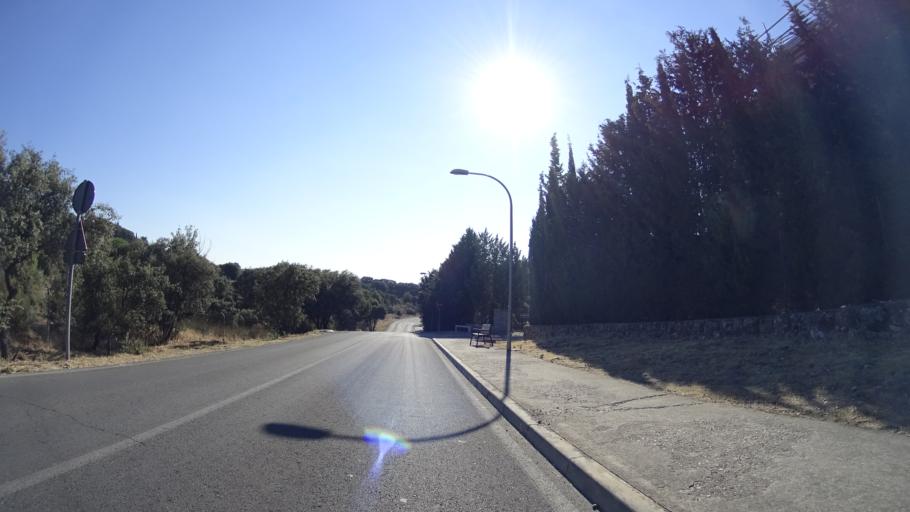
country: ES
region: Madrid
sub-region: Provincia de Madrid
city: Torrelodones
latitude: 40.5821
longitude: -3.9045
